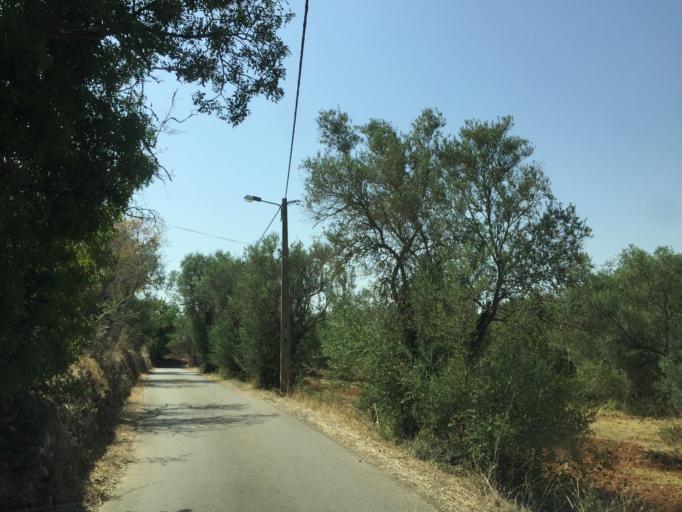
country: PT
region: Faro
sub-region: Loule
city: Boliqueime
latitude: 37.1103
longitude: -8.1890
